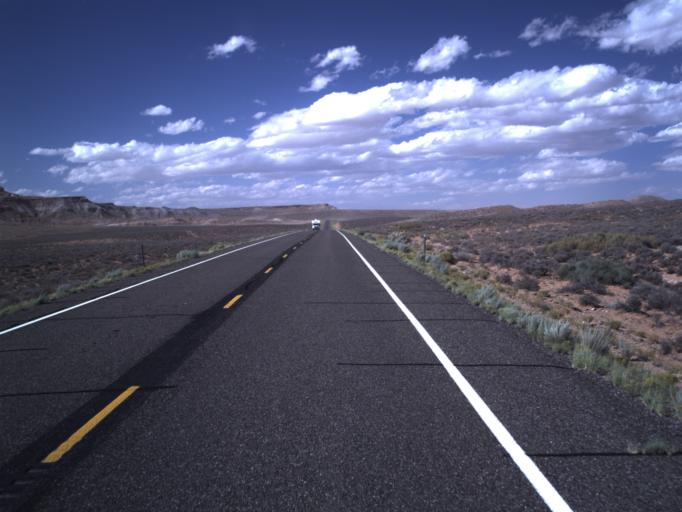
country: US
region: Utah
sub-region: Wayne County
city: Loa
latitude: 38.0860
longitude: -110.6153
